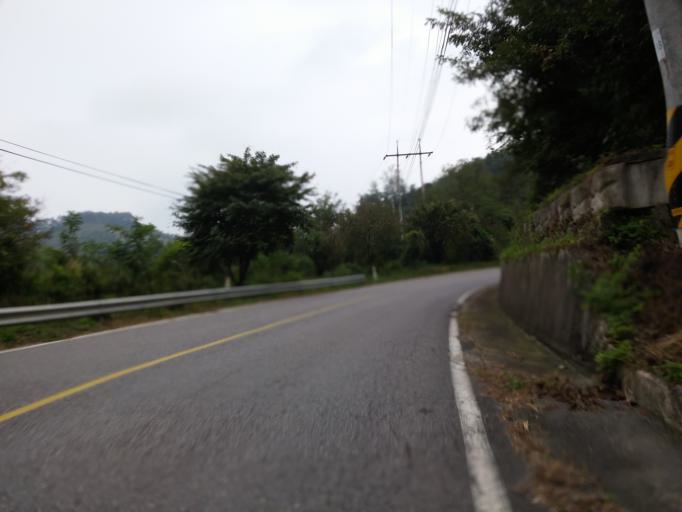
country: KR
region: Chungcheongbuk-do
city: Okcheon
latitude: 36.3971
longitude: 127.6785
